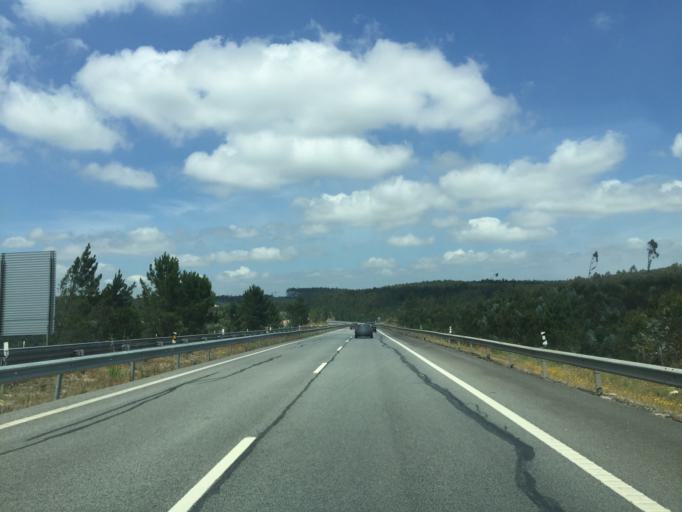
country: PT
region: Leiria
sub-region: Bombarral
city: Bombarral
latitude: 39.2022
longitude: -9.1924
